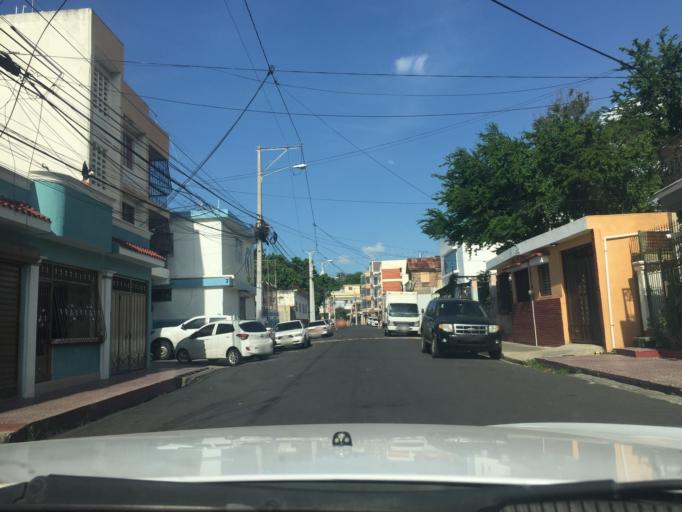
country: DO
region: Santiago
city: Santiago de los Caballeros
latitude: 19.4552
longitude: -70.7097
